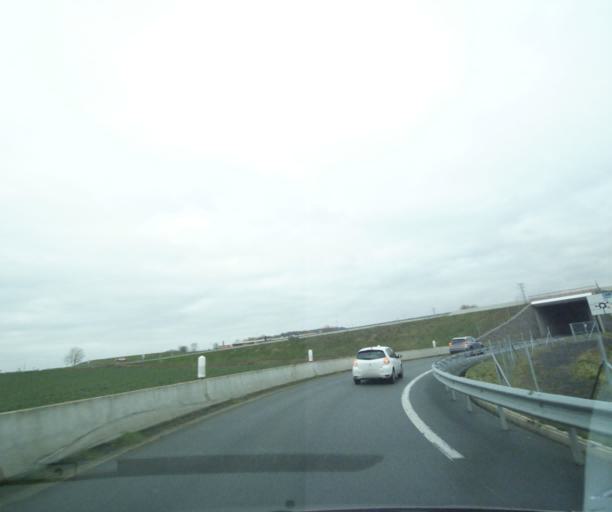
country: FR
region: Picardie
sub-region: Departement de l'Oise
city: Noyon
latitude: 49.5674
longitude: 2.9806
